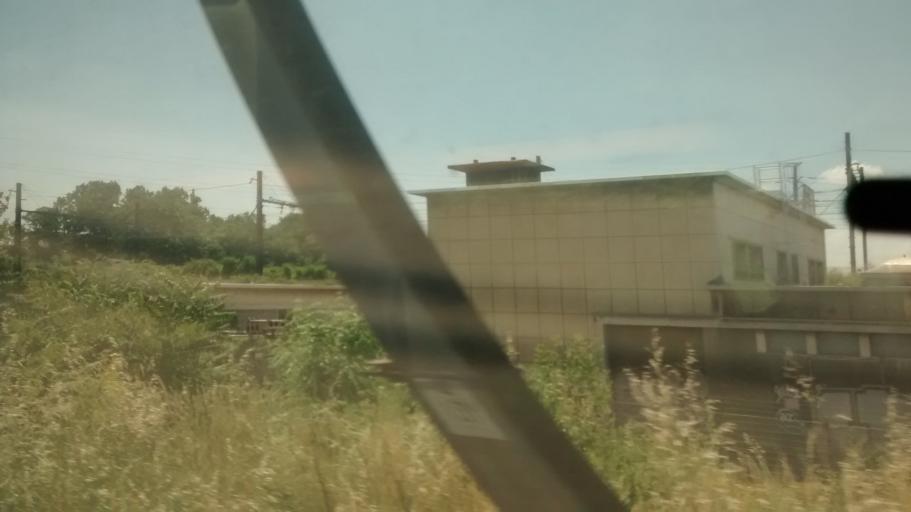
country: FR
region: Rhone-Alpes
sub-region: Departement du Rhone
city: Saint-Fons
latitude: 45.7184
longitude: 4.8502
